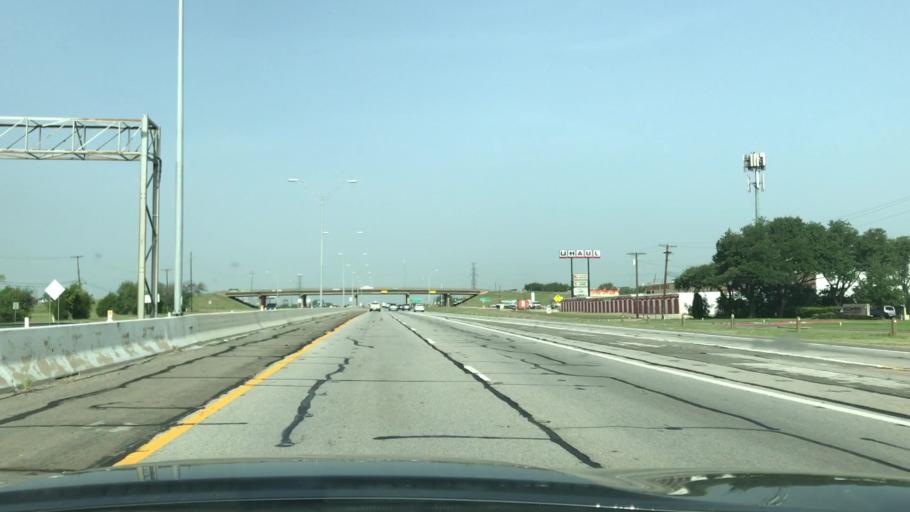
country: US
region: Texas
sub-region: Dallas County
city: Mesquite
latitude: 32.7925
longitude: -96.6304
